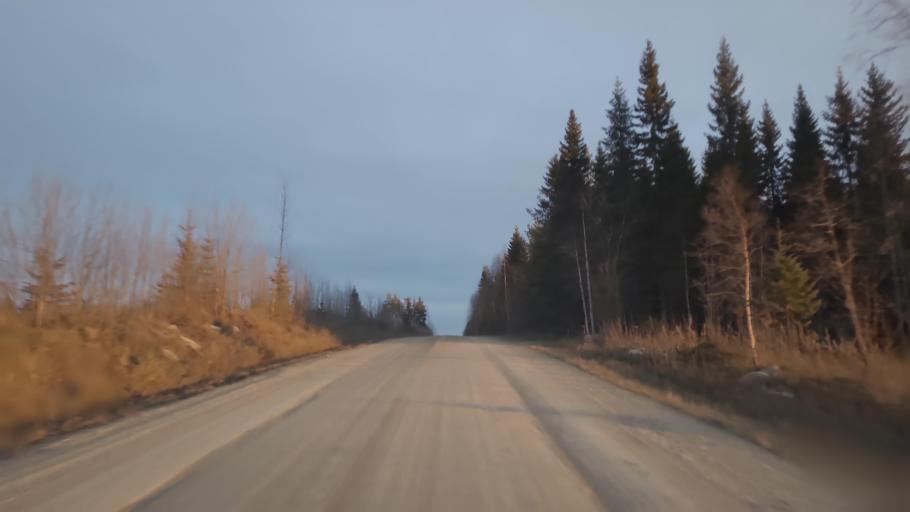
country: FI
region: Lapland
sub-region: Kemi-Tornio
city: Tervola
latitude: 66.0605
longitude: 24.9323
